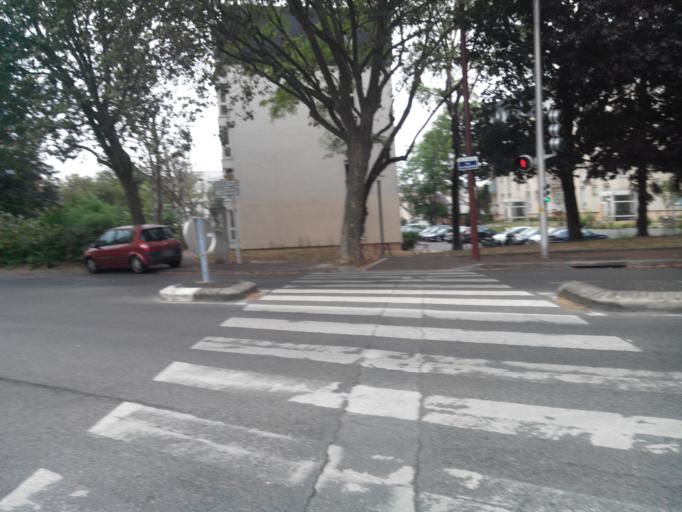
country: FR
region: Ile-de-France
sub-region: Departement du Val-de-Marne
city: L'Hay-les-Roses
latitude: 48.7885
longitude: 2.3328
